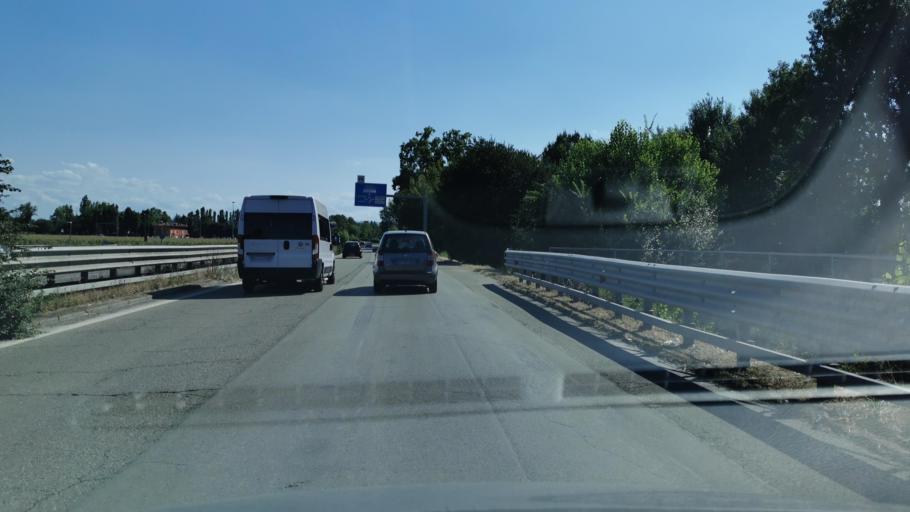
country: IT
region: Emilia-Romagna
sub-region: Provincia di Modena
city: Modena
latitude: 44.6281
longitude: 10.9522
